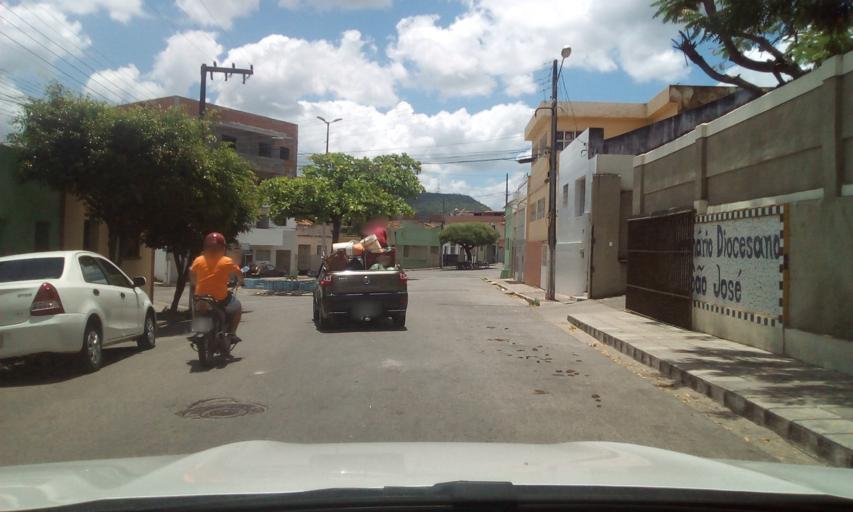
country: BR
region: Paraiba
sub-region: Guarabira
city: Guarabira
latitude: -6.8536
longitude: -35.4877
